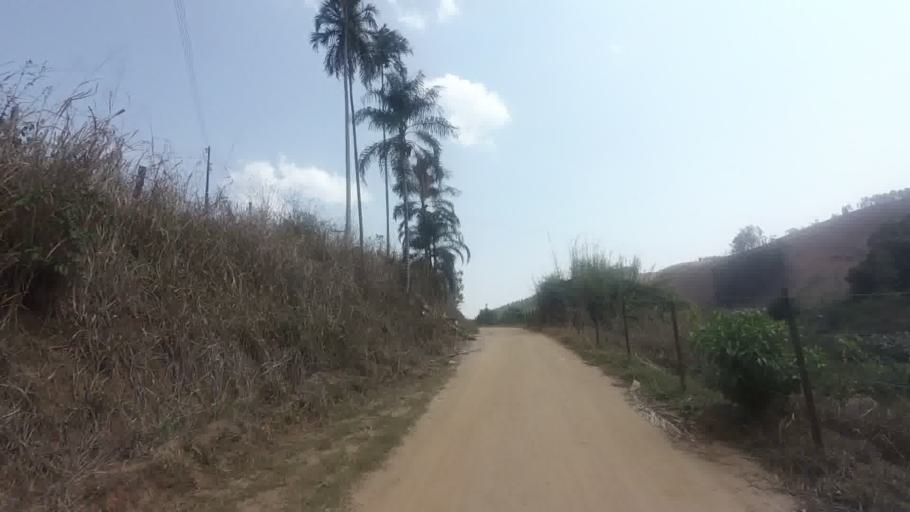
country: BR
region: Espirito Santo
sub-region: Sao Jose Do Calcado
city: Sao Jose do Calcado
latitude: -21.0451
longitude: -41.5222
